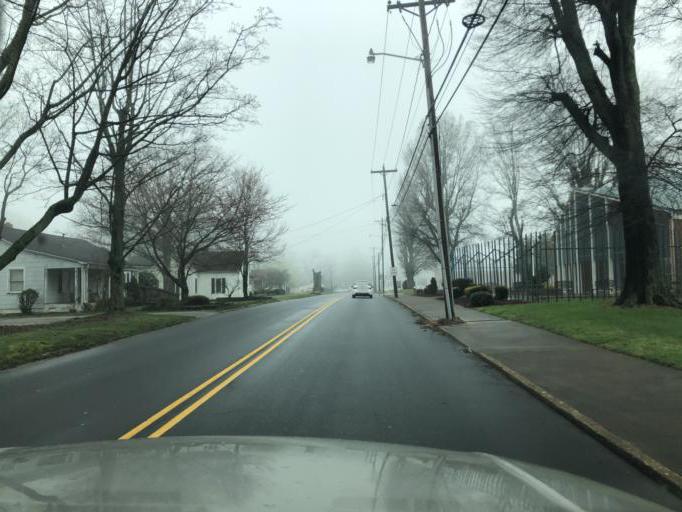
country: US
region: North Carolina
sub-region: Gaston County
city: Cherryville
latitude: 35.3809
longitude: -81.3837
